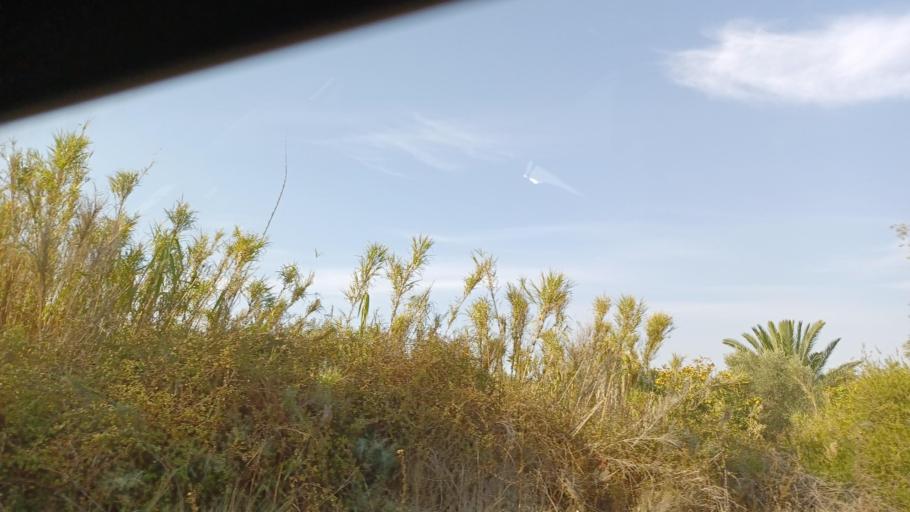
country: CY
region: Larnaka
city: Mosfiloti
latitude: 34.9675
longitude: 33.4287
